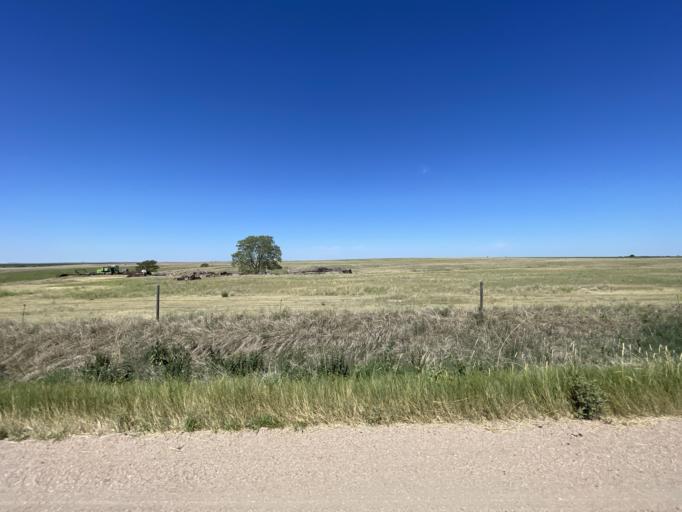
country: US
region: Nebraska
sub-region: Red Willow County
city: McCook
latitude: 40.4339
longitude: -100.7303
